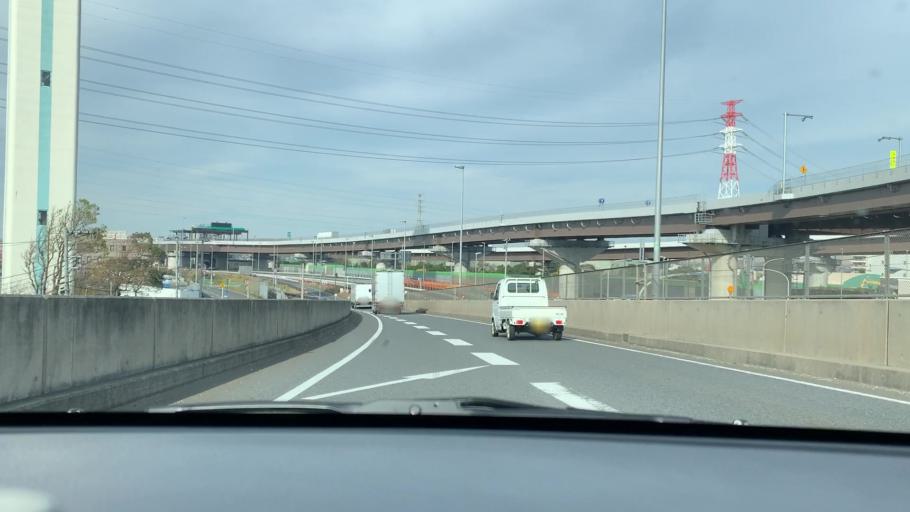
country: JP
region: Chiba
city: Funabashi
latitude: 35.6876
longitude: 139.9447
